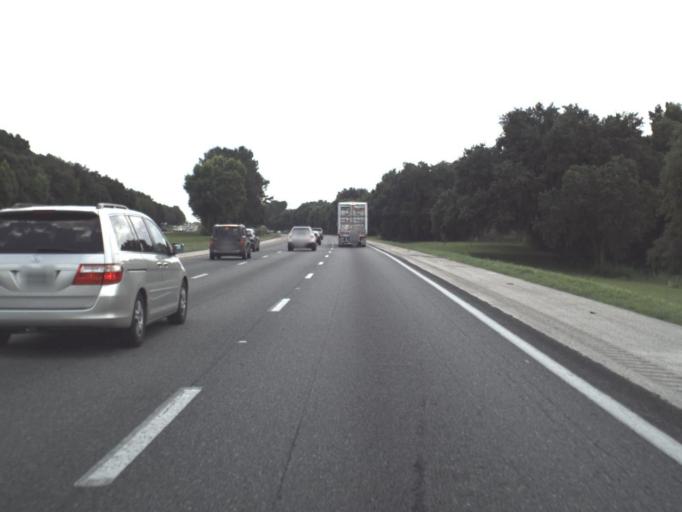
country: US
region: Florida
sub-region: Alachua County
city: Gainesville
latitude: 29.5565
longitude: -82.3436
